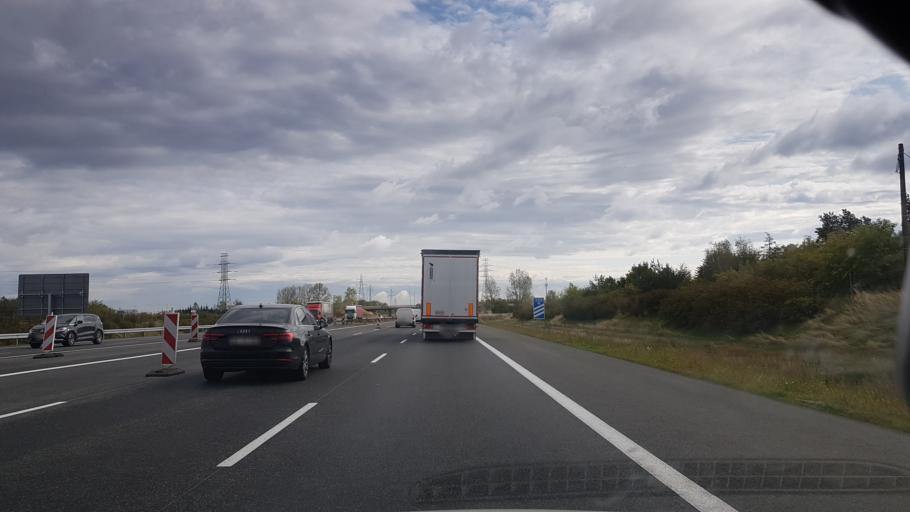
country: PL
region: Greater Poland Voivodeship
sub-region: Powiat poznanski
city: Komorniki
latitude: 52.3505
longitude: 16.8182
